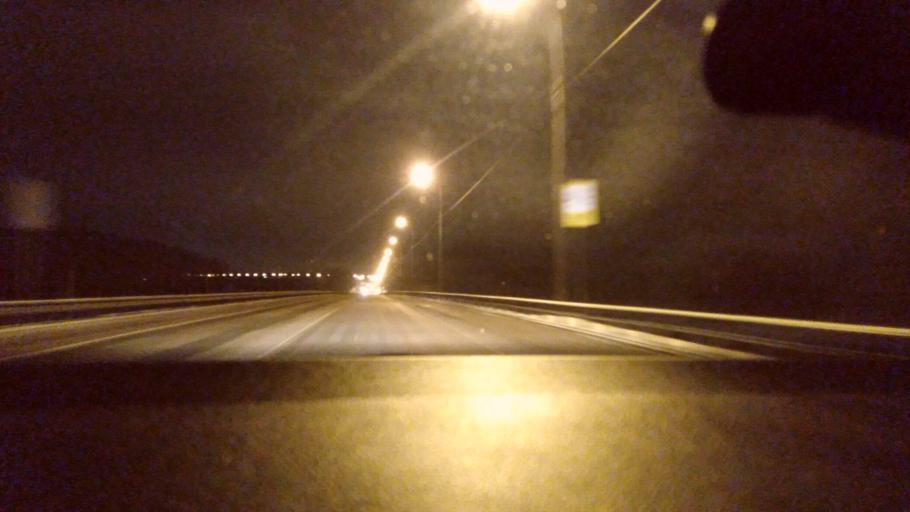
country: RU
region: Moskovskaya
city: Troitskoye
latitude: 55.2339
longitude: 38.5494
